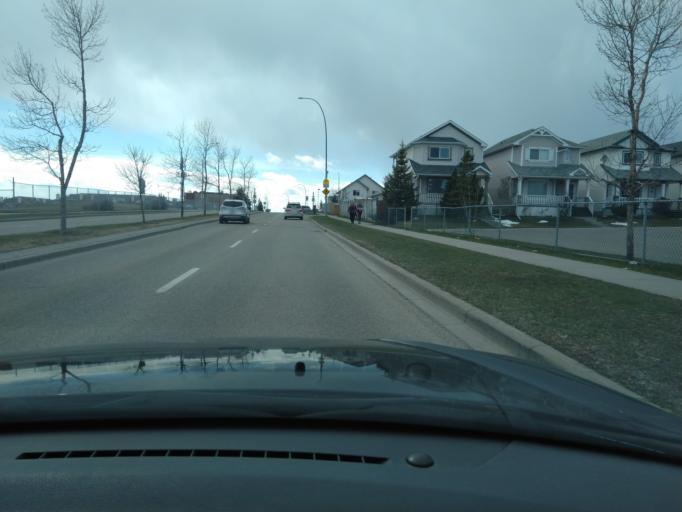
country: CA
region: Alberta
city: Calgary
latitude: 51.1341
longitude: -114.2067
